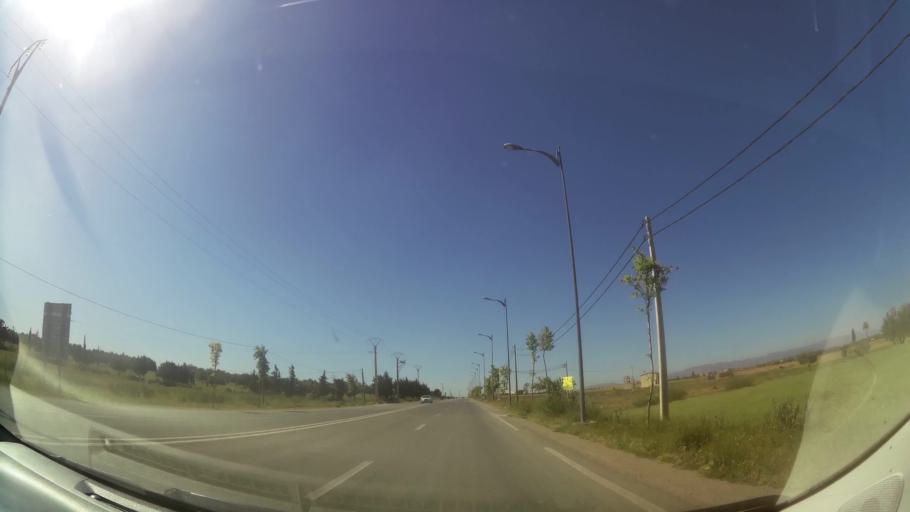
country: MA
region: Oriental
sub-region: Oujda-Angad
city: Oujda
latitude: 34.7218
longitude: -1.8662
